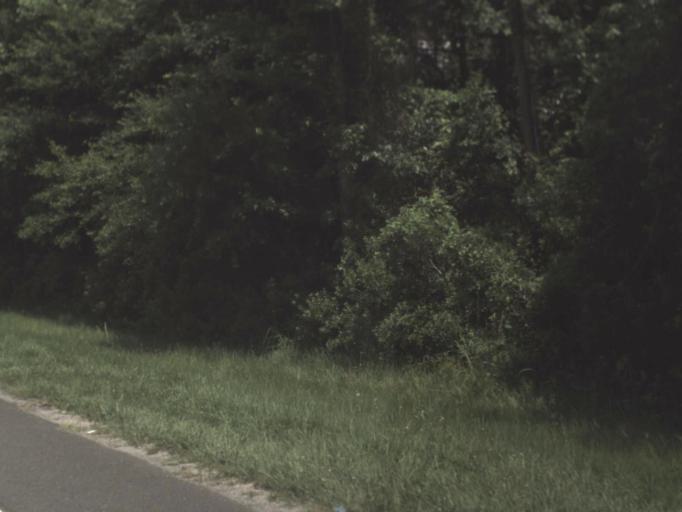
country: US
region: Florida
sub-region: Nassau County
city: Nassau Village-Ratliff
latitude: 30.5485
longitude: -81.7849
